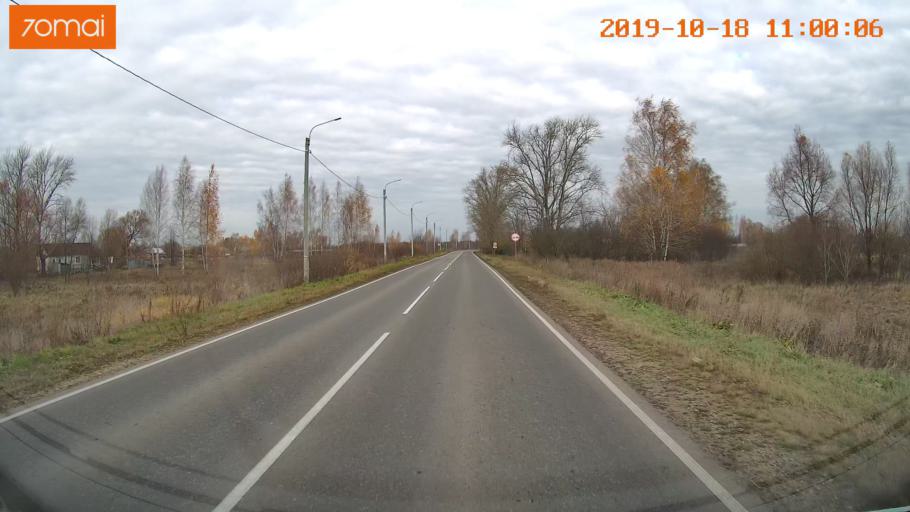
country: RU
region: Tula
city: Yepifan'
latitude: 53.8389
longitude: 38.5536
